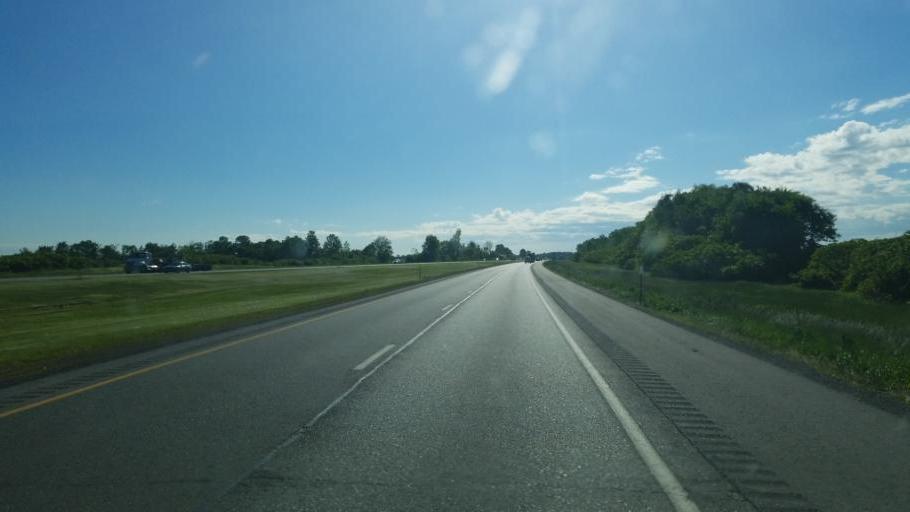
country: US
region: New York
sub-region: Genesee County
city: Le Roy
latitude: 43.0299
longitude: -78.0338
